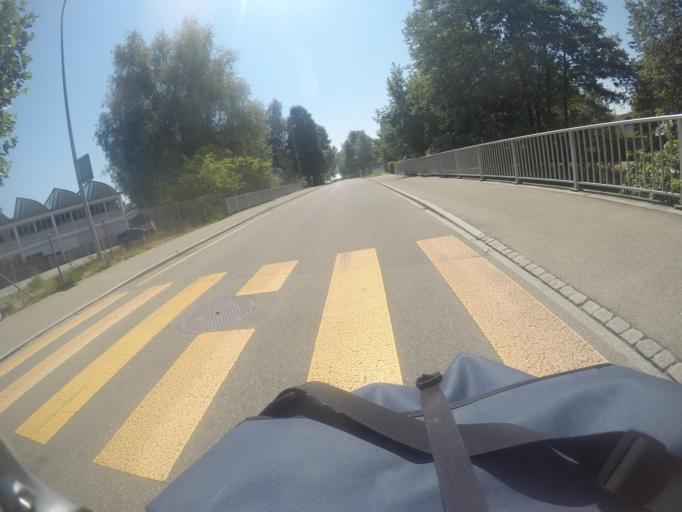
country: CH
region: Thurgau
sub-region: Arbon District
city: Arbon
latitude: 47.5066
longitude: 9.4286
